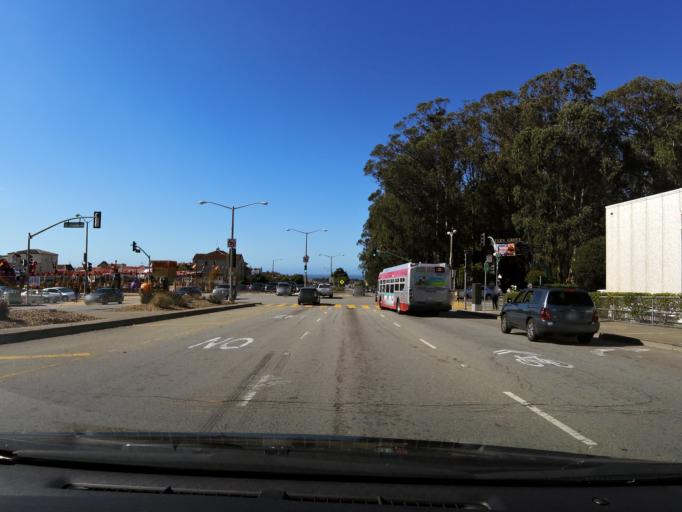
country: US
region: California
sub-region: San Mateo County
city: Daly City
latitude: 37.7347
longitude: -122.4744
